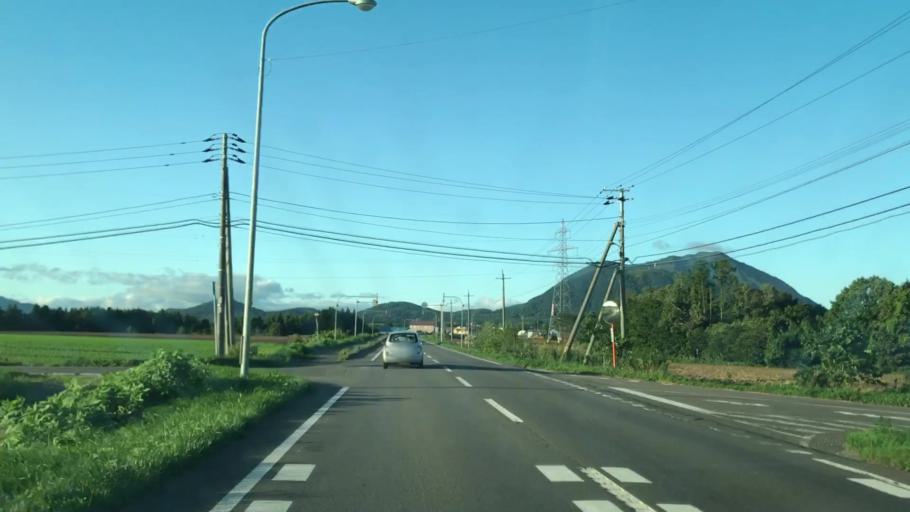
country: JP
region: Hokkaido
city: Niseko Town
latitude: 42.7189
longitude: 140.8599
